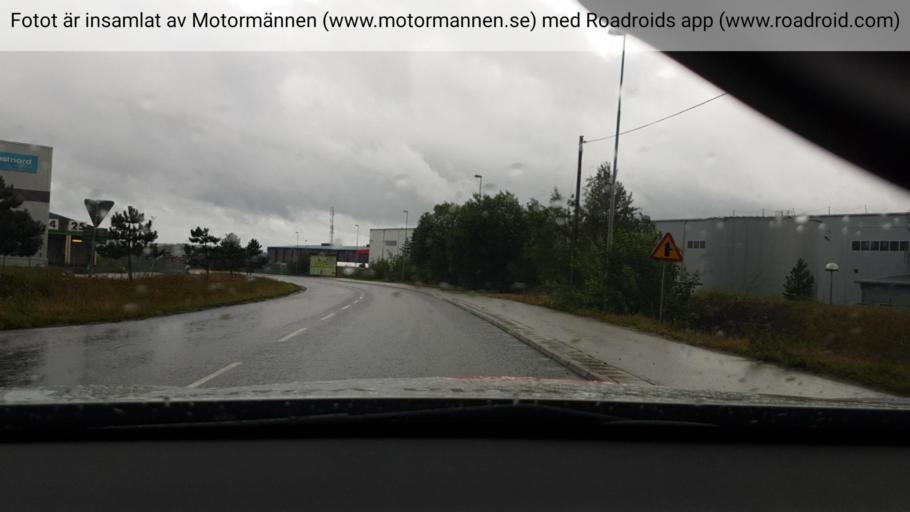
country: SE
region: Stockholm
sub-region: Haninge Kommun
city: Jordbro
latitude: 59.1585
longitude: 18.1113
